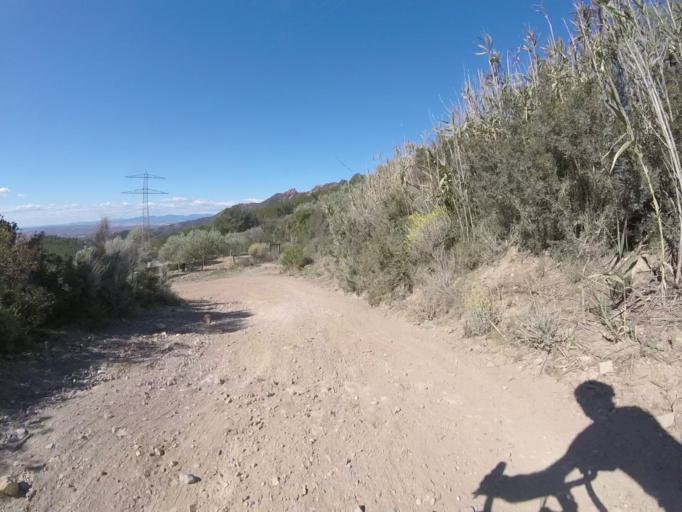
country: ES
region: Valencia
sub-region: Provincia de Castello
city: Benicassim
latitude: 40.0819
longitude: 0.0833
